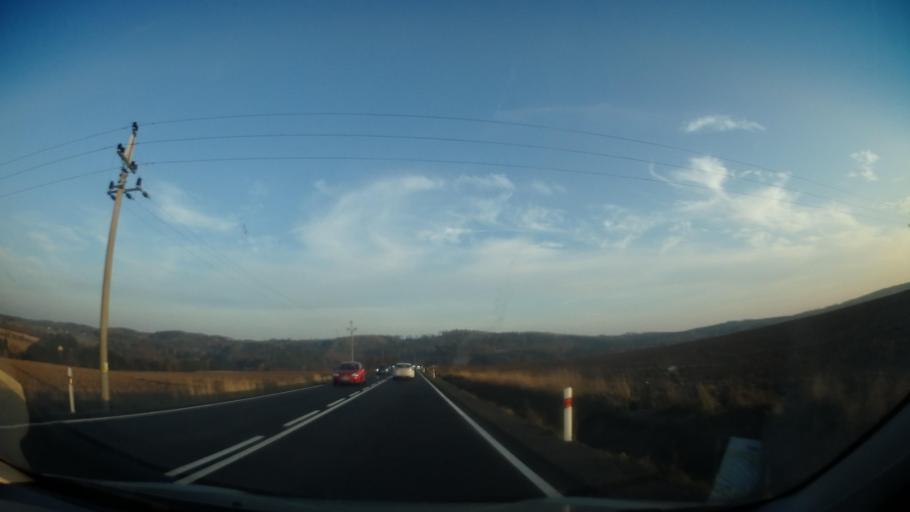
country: CZ
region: Central Bohemia
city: Postupice
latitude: 49.7355
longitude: 14.8214
